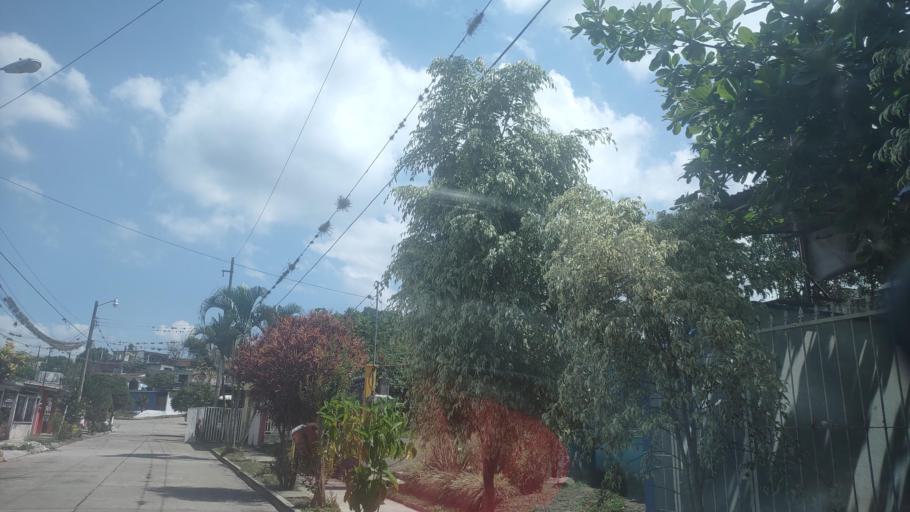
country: MX
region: Veracruz
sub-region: Coatepec
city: Las Lomas
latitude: 19.4075
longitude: -96.9143
